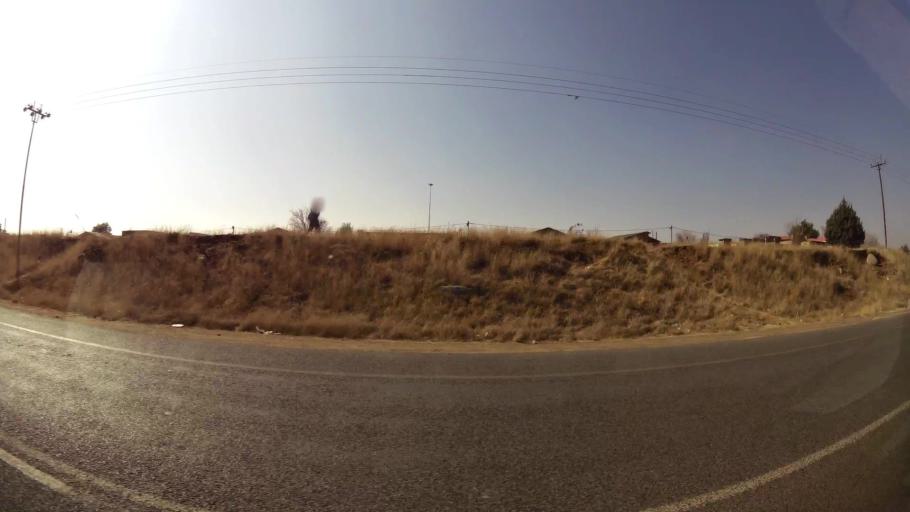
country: ZA
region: Orange Free State
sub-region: Mangaung Metropolitan Municipality
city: Bloemfontein
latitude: -29.1838
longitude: 26.2685
